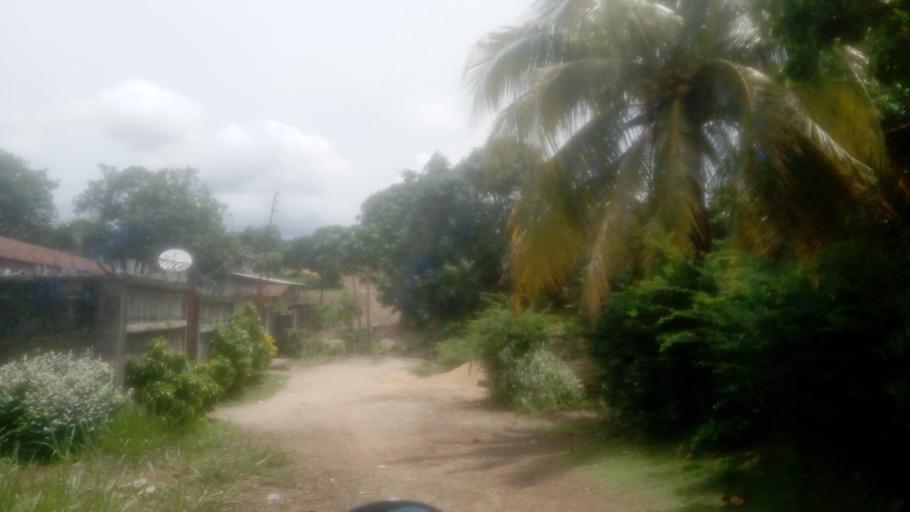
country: SL
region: Southern Province
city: Bo
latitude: 7.9541
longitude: -11.7101
